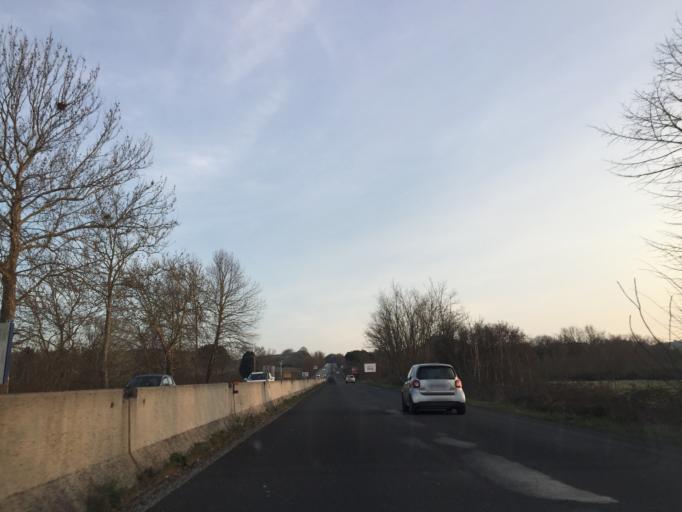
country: IT
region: Latium
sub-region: Citta metropolitana di Roma Capitale
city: Campagnano di Roma
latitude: 42.1465
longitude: 12.3500
